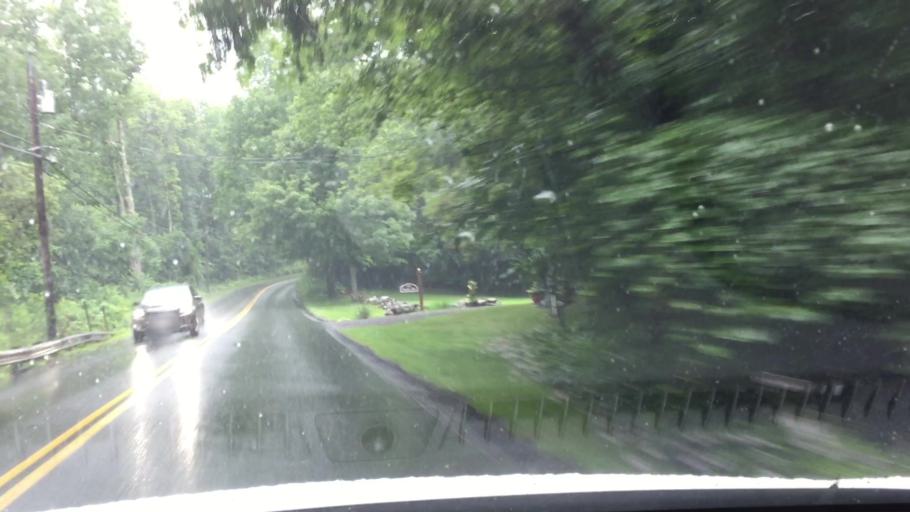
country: US
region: Massachusetts
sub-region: Berkshire County
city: Lanesborough
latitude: 42.5419
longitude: -73.2356
